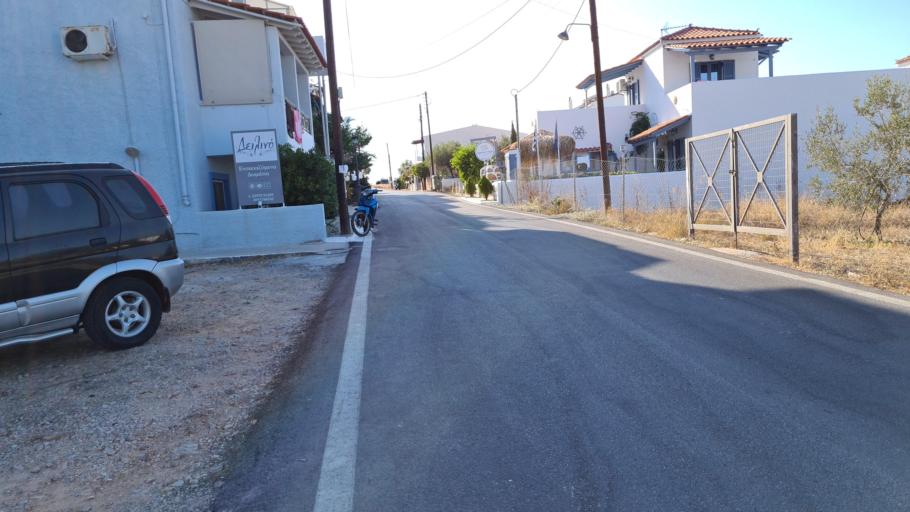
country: GR
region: Attica
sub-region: Nomos Piraios
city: Megalochori
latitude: 37.7088
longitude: 23.3602
